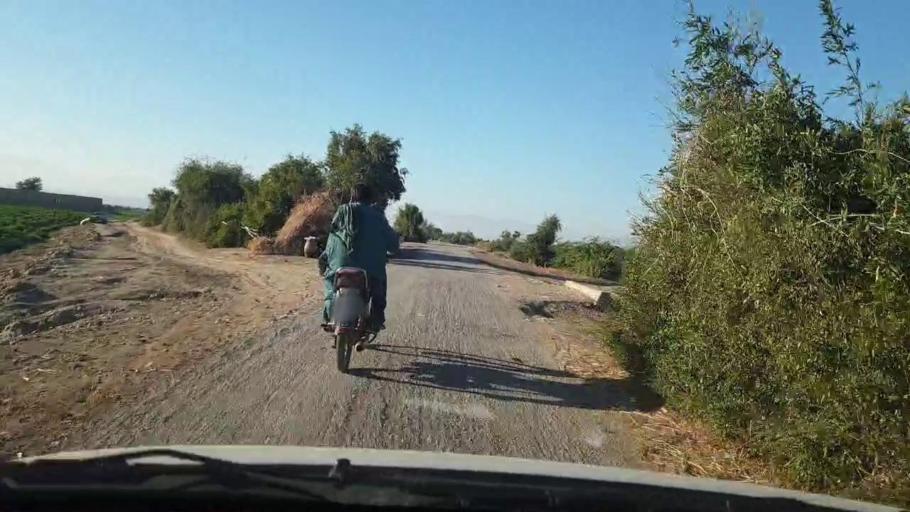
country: PK
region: Sindh
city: Johi
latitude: 26.7657
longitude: 67.4634
